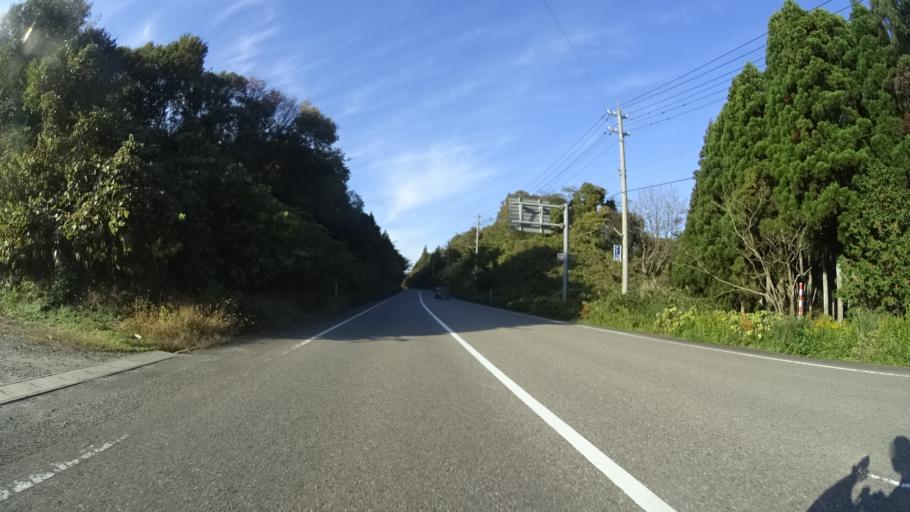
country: JP
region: Ishikawa
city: Hakui
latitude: 37.0089
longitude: 136.7996
